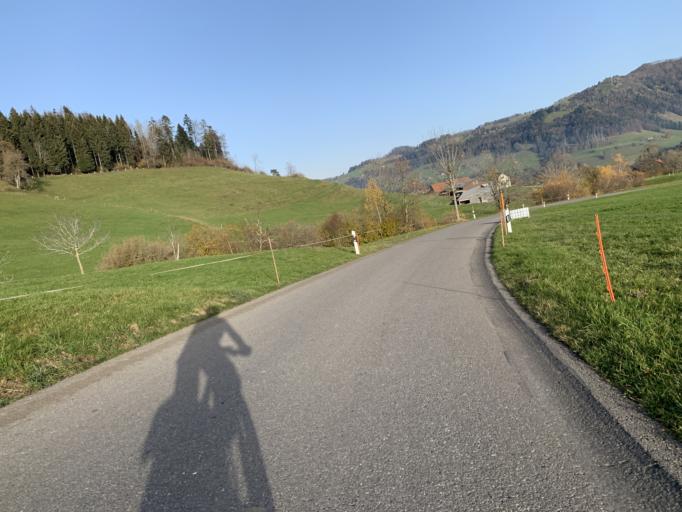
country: CH
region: Zurich
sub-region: Bezirk Hinwil
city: Wald
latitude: 47.3114
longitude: 8.8951
